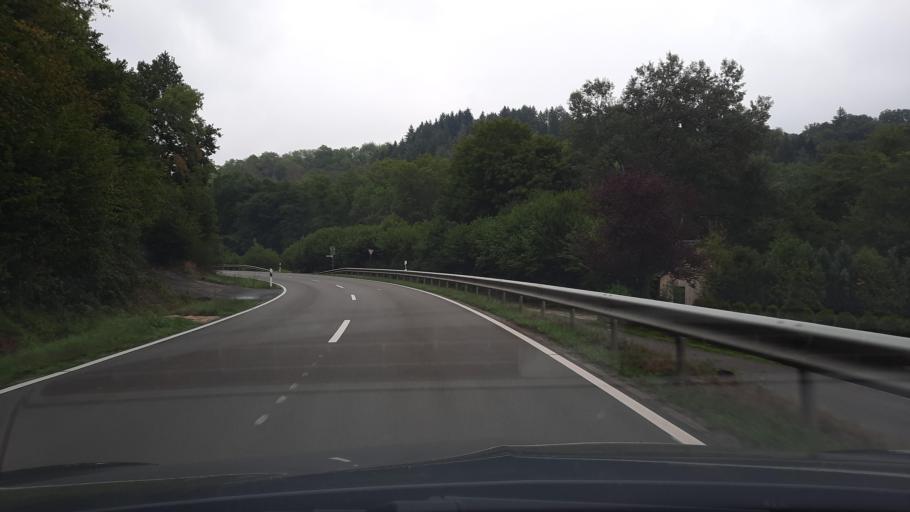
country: DE
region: Rheinland-Pfalz
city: Morscheid
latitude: 49.7299
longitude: 6.7386
